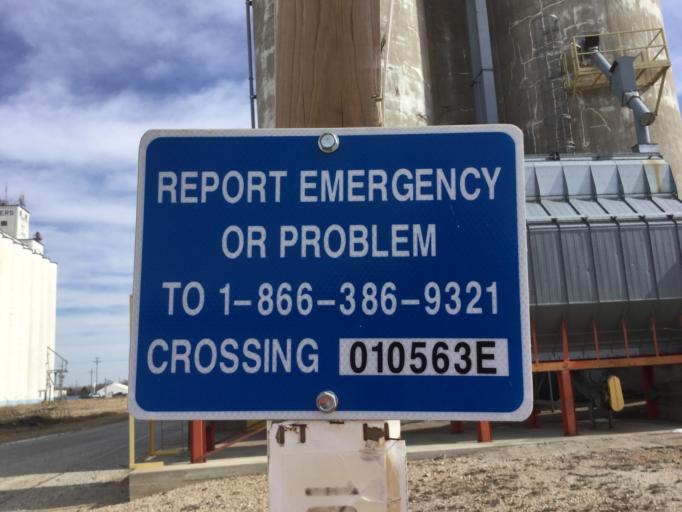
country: US
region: Kansas
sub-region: Rice County
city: Lyons
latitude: 38.3510
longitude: -98.2046
